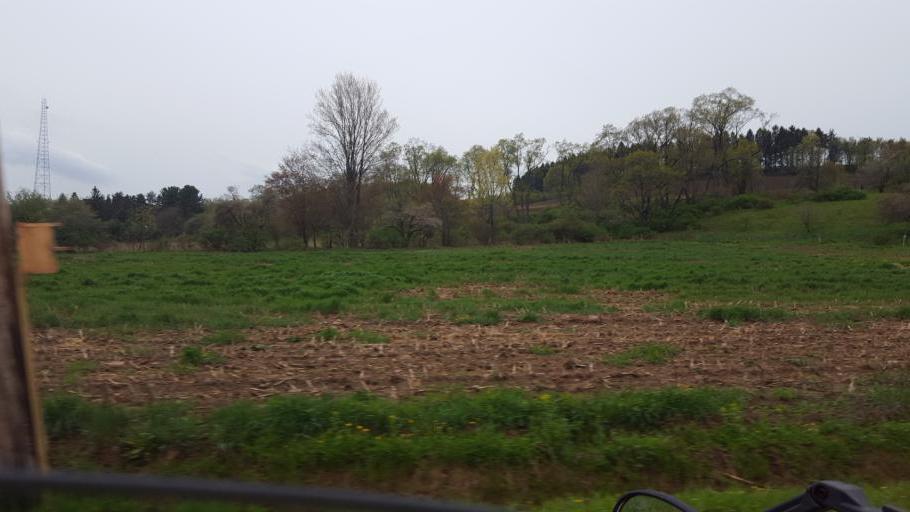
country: US
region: Pennsylvania
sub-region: Tioga County
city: Westfield
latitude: 41.9200
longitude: -77.7510
